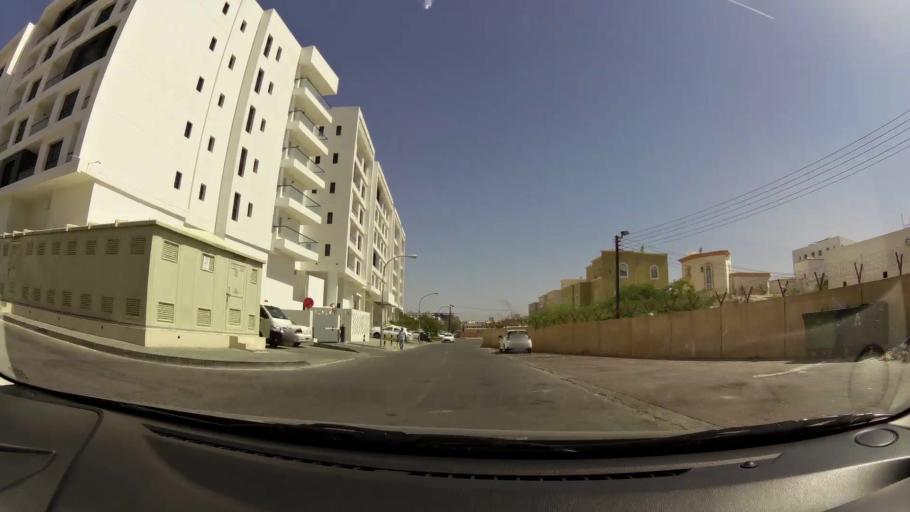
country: OM
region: Muhafazat Masqat
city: Bawshar
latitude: 23.5939
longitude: 58.3627
